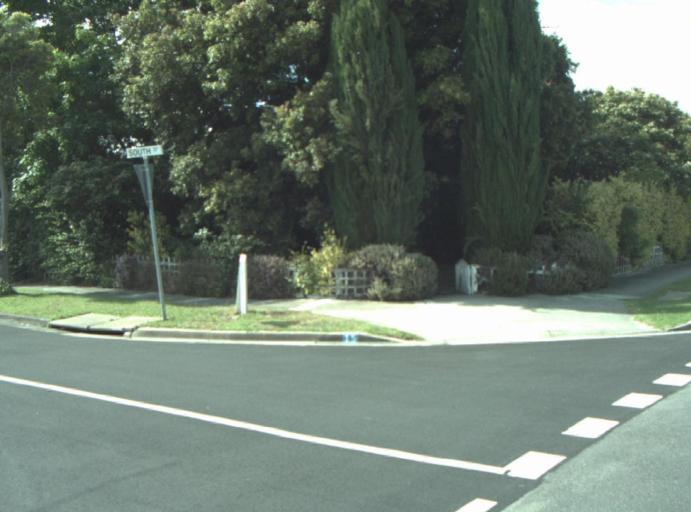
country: AU
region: Victoria
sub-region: Greater Geelong
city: Wandana Heights
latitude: -38.1735
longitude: 144.3355
